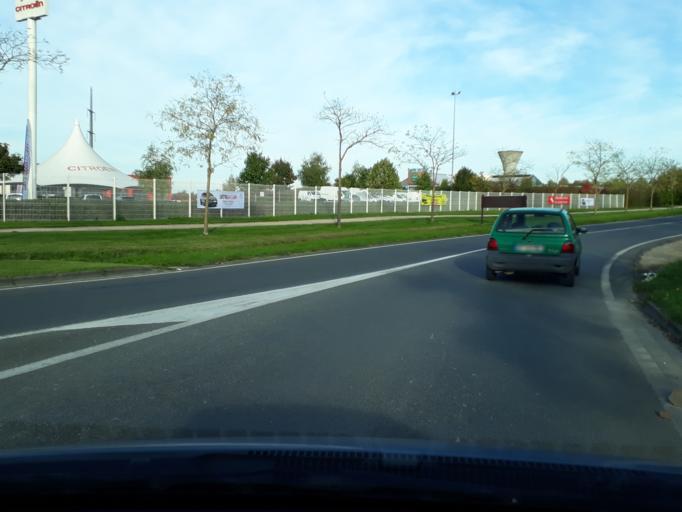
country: FR
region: Ile-de-France
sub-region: Departement de Seine-et-Marne
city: Ecuelles
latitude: 48.3677
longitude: 2.8402
